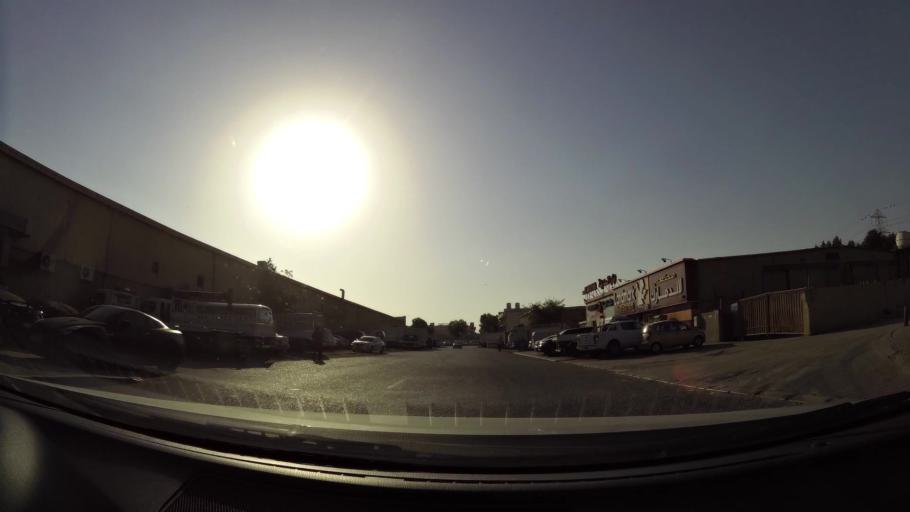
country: AE
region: Dubai
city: Dubai
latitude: 25.1325
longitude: 55.2420
